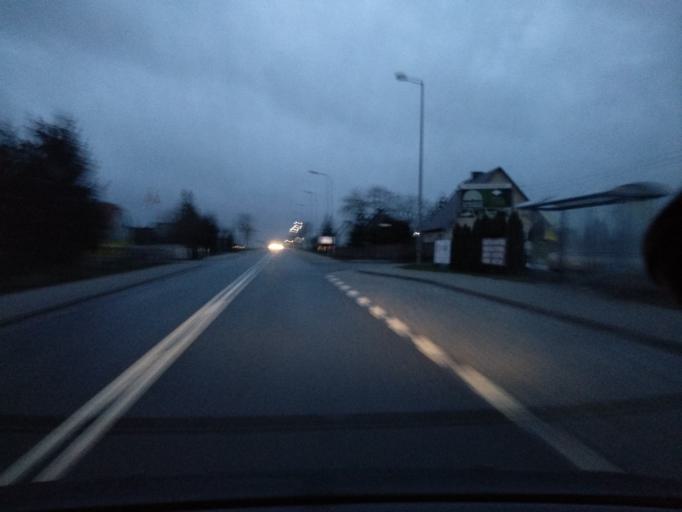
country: PL
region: Lower Silesian Voivodeship
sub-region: Powiat sredzki
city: Miekinia
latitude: 51.1599
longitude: 16.7226
